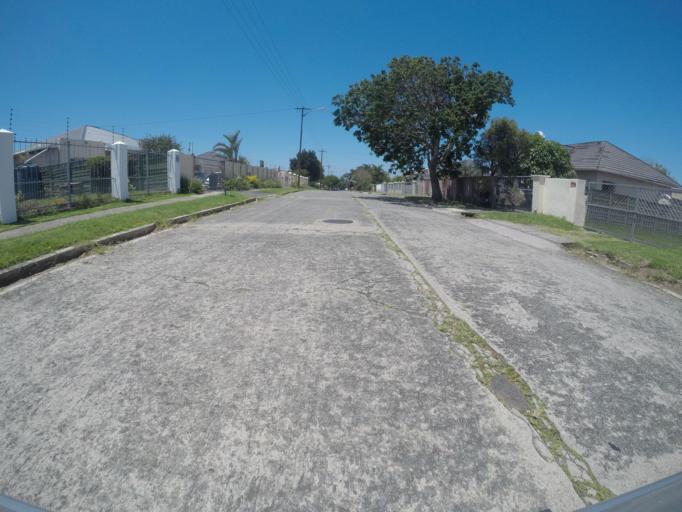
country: ZA
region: Eastern Cape
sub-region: Buffalo City Metropolitan Municipality
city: East London
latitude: -32.9886
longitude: 27.9071
